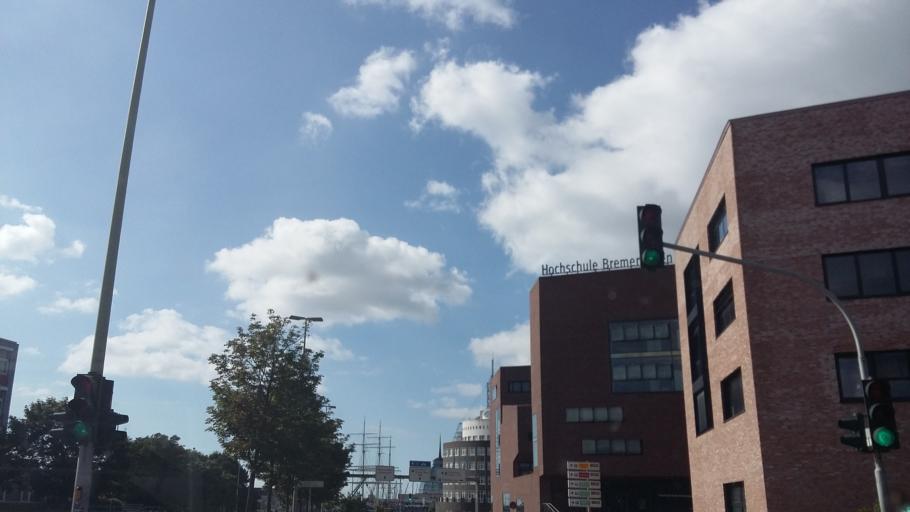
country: DE
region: Bremen
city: Bremerhaven
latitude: 53.5389
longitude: 8.5830
